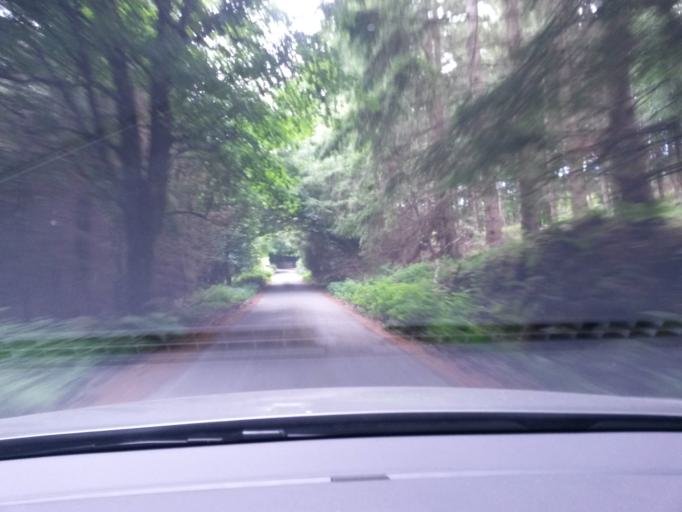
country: IE
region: Leinster
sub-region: Wicklow
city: Enniskerry
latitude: 53.1660
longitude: -6.2199
